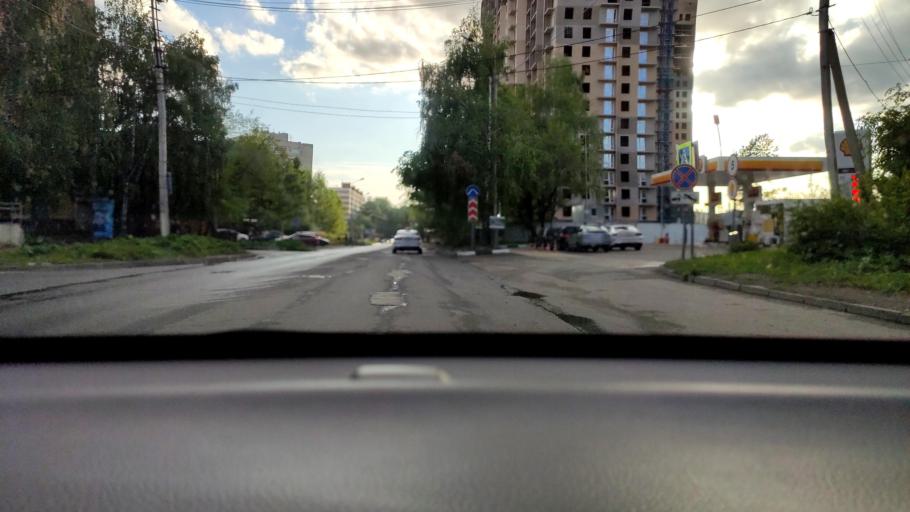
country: RU
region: Tatarstan
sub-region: Gorod Kazan'
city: Kazan
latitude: 55.7577
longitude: 49.2006
